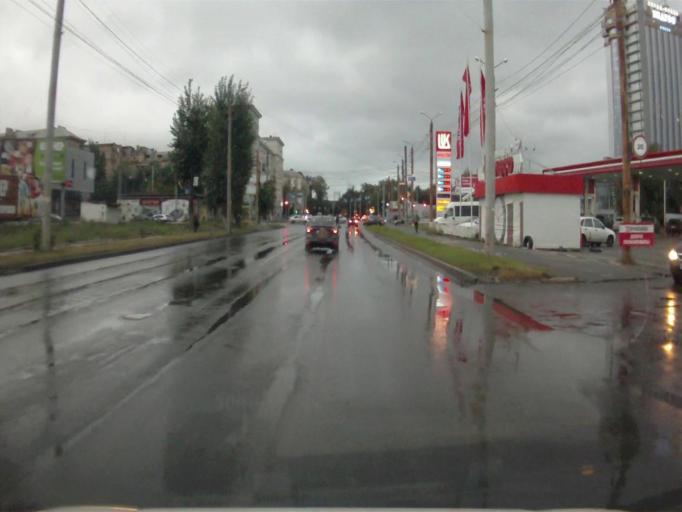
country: RU
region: Chelyabinsk
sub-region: Gorod Chelyabinsk
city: Chelyabinsk
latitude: 55.1637
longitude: 61.4341
